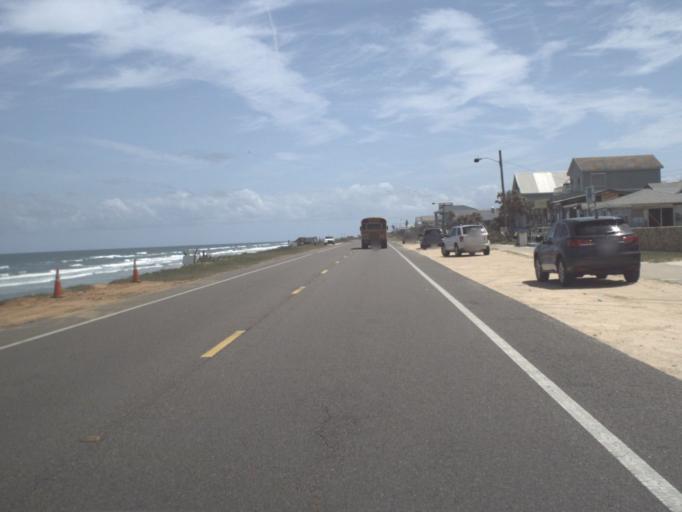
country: US
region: Florida
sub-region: Flagler County
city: Flagler Beach
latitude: 29.5071
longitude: -81.1401
